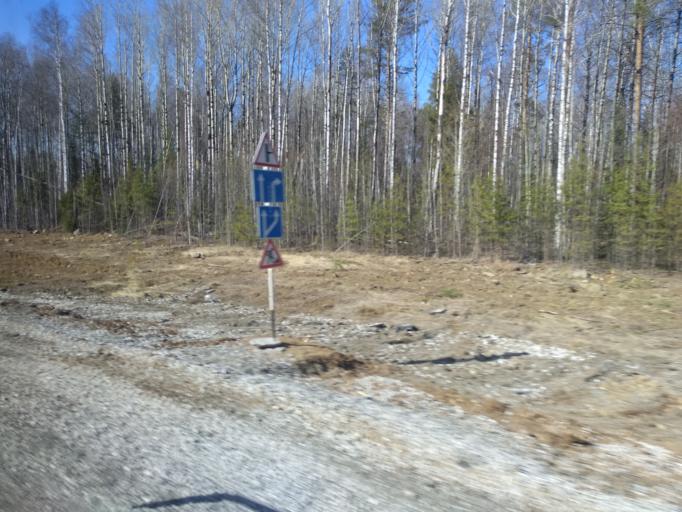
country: RU
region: Sverdlovsk
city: Krasnotur'insk
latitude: 59.6685
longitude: 60.1853
